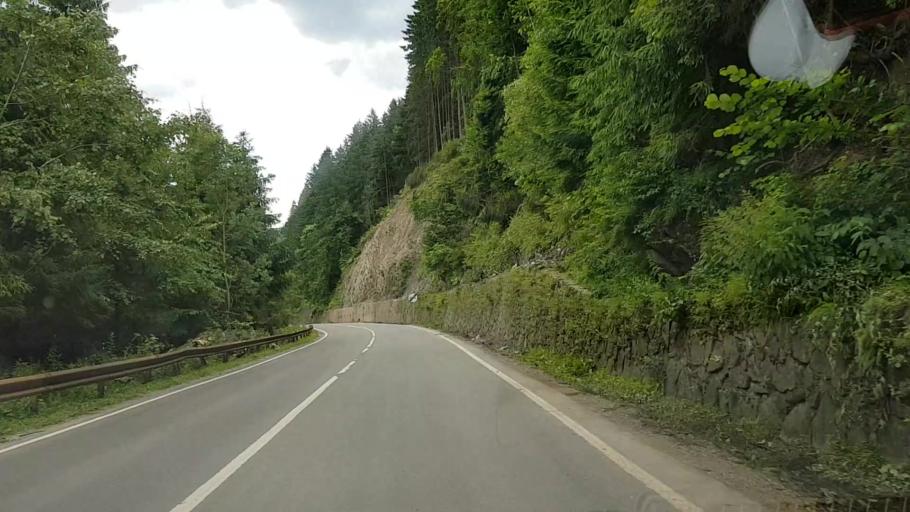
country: RO
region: Neamt
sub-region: Comuna Poiana Teiului
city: Poiana Teiului
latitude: 47.0931
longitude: 25.9490
